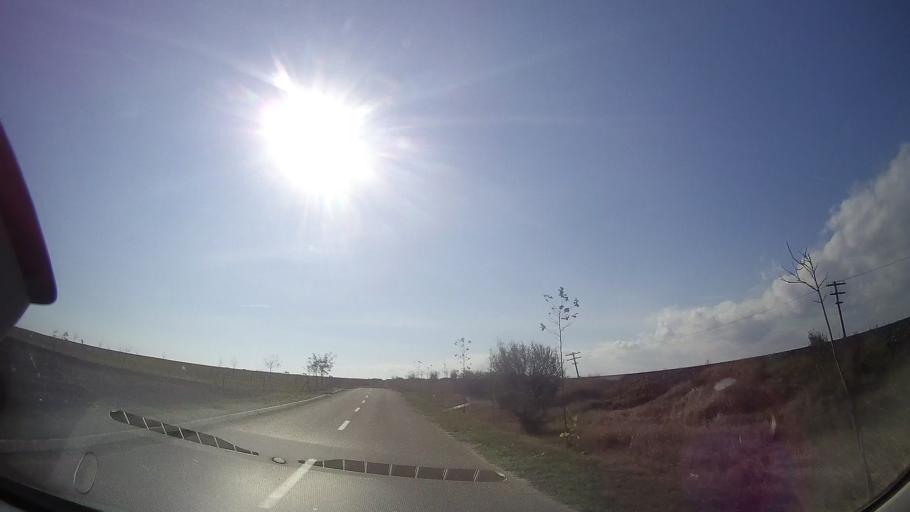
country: RO
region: Constanta
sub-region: Comuna Costinesti
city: Schitu
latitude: 43.9228
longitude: 28.6316
